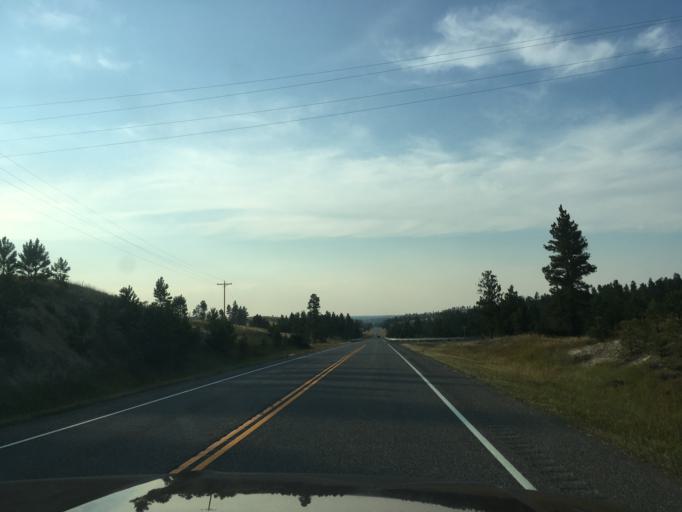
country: US
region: Montana
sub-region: Musselshell County
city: Roundup
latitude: 46.2623
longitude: -108.4669
